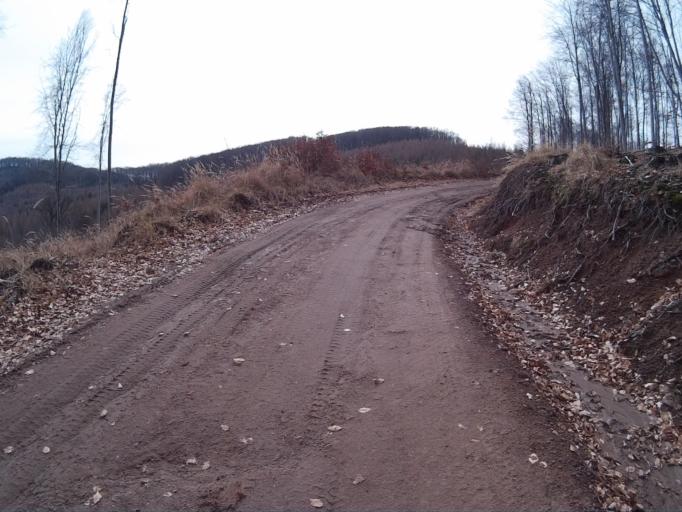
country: HU
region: Borsod-Abauj-Zemplen
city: Tolcsva
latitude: 48.4031
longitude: 21.4208
